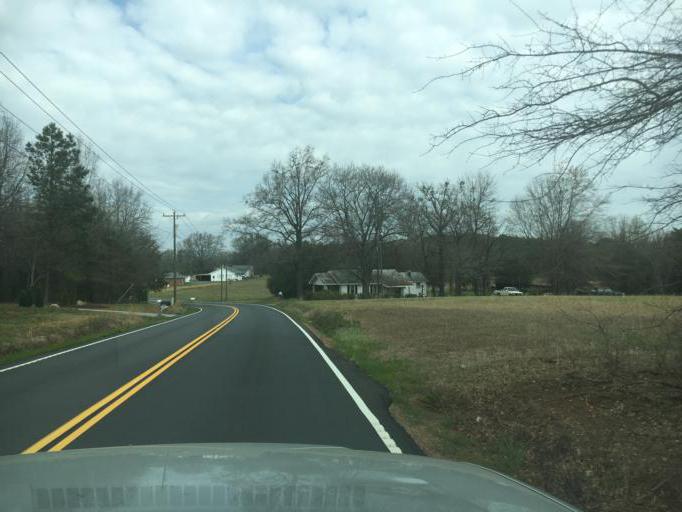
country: US
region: South Carolina
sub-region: Spartanburg County
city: Inman Mills
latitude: 35.0765
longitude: -82.1816
